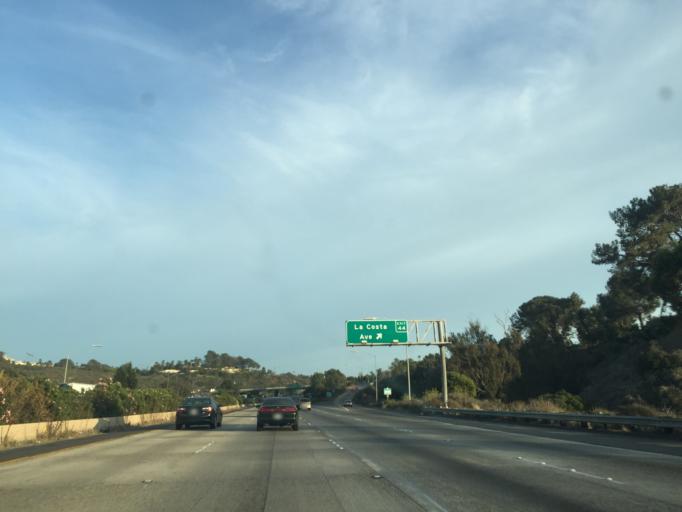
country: US
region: California
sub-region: San Diego County
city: Encinitas
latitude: 33.0884
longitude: -117.3010
